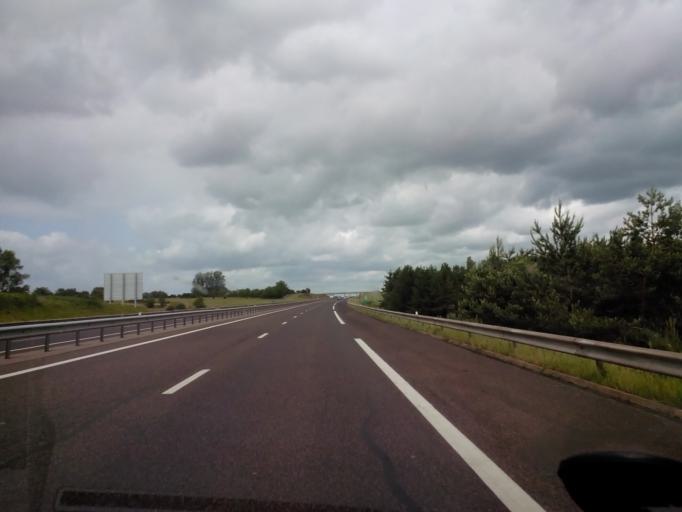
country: FR
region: Lorraine
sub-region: Departement de Meurthe-et-Moselle
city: Blenod-les-Toul
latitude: 48.5782
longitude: 5.8864
